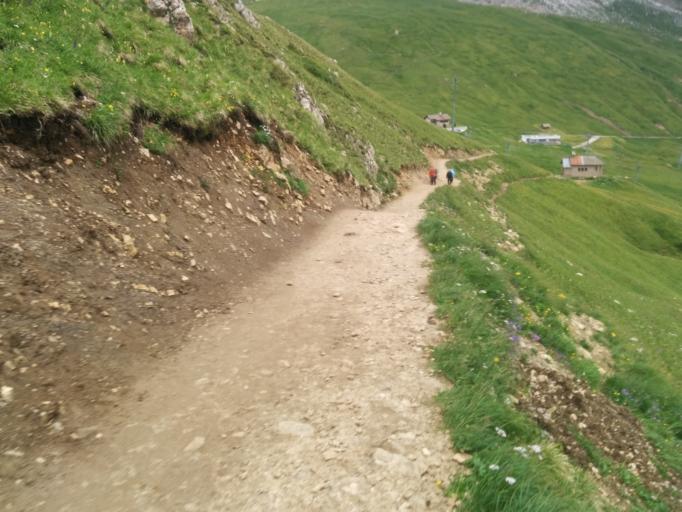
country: IT
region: Trentino-Alto Adige
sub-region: Provincia di Trento
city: Canazei
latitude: 46.4845
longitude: 11.8135
